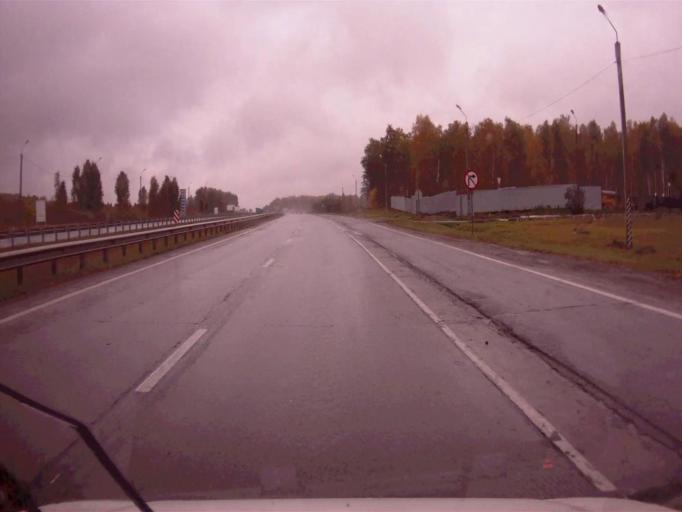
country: RU
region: Chelyabinsk
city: Dolgoderevenskoye
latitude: 55.3264
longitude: 61.3281
